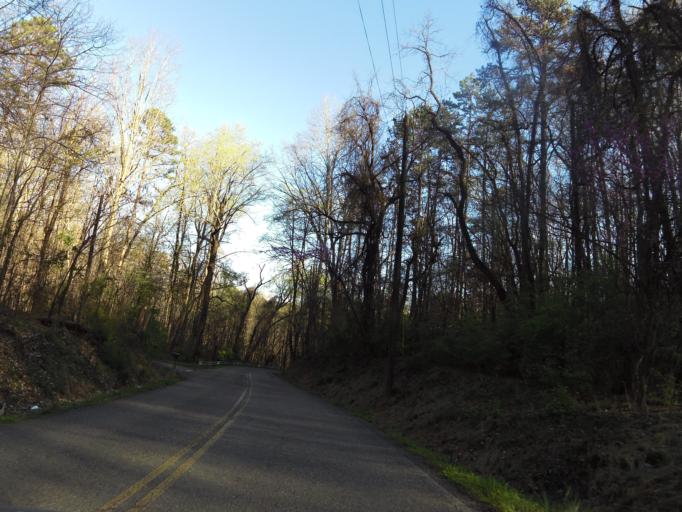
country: US
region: Tennessee
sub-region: Knox County
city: Mascot
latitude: 35.9796
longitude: -83.7554
